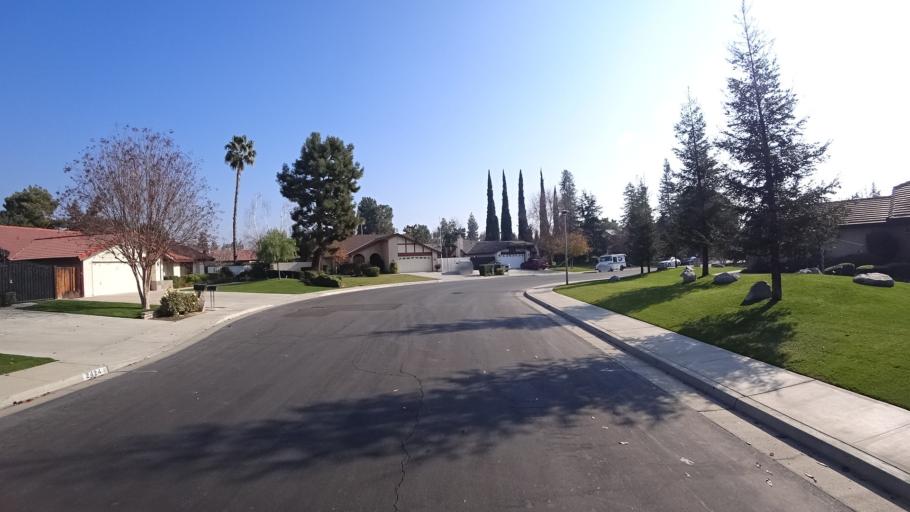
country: US
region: California
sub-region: Kern County
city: Greenacres
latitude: 35.3328
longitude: -119.0826
